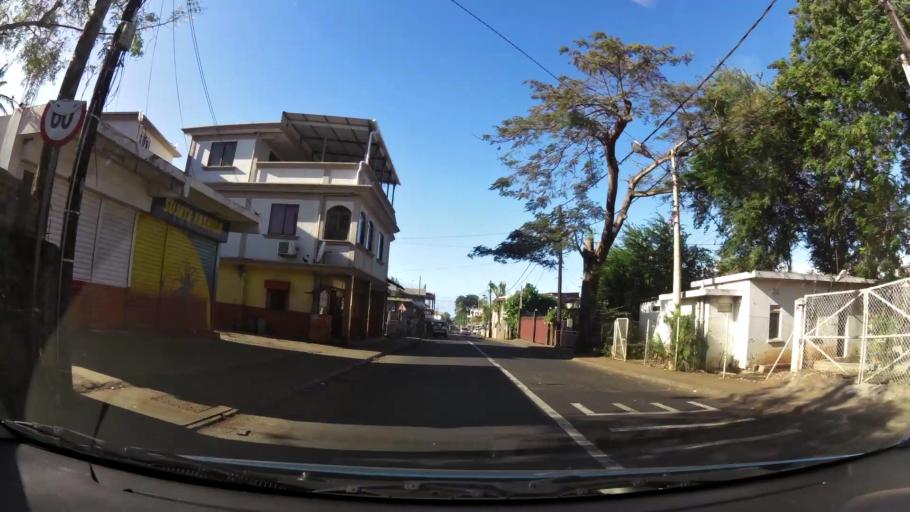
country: MU
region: Black River
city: Petite Riviere
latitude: -20.1958
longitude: 57.4466
